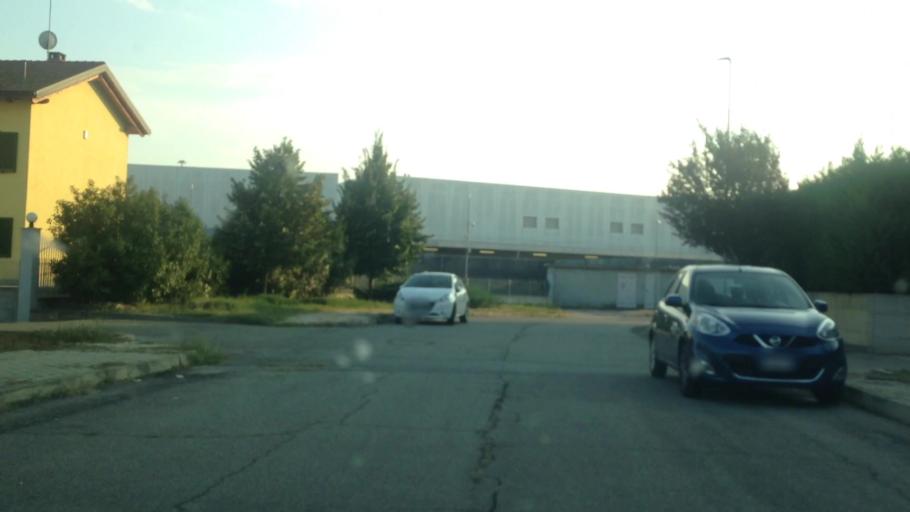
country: IT
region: Piedmont
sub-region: Provincia di Asti
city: Asti
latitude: 44.9167
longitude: 8.2251
